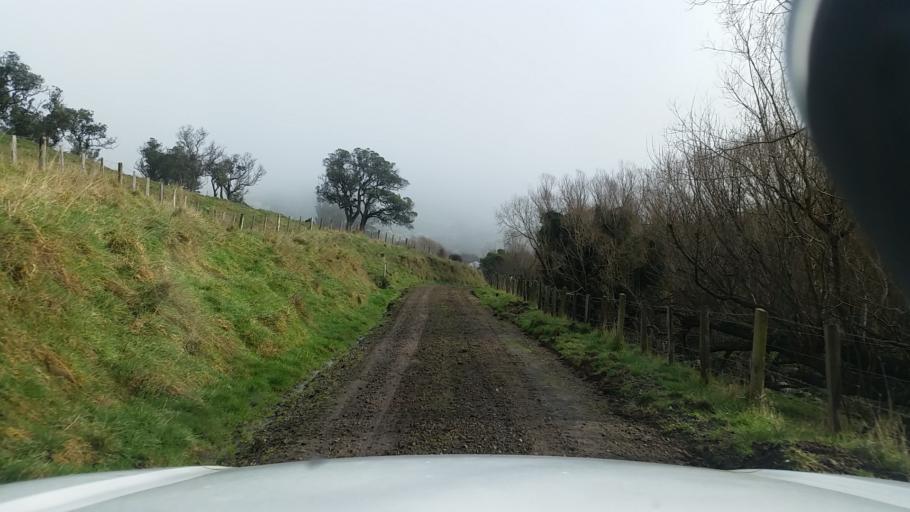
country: NZ
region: Canterbury
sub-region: Christchurch City
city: Christchurch
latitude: -43.6924
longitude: 172.9165
